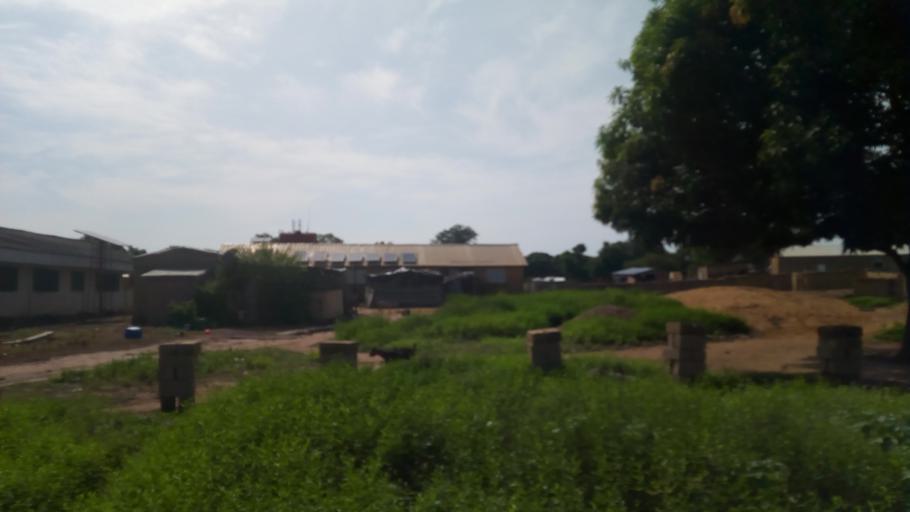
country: ML
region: Koulikoro
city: Kangaba
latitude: 11.6797
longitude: -8.7131
